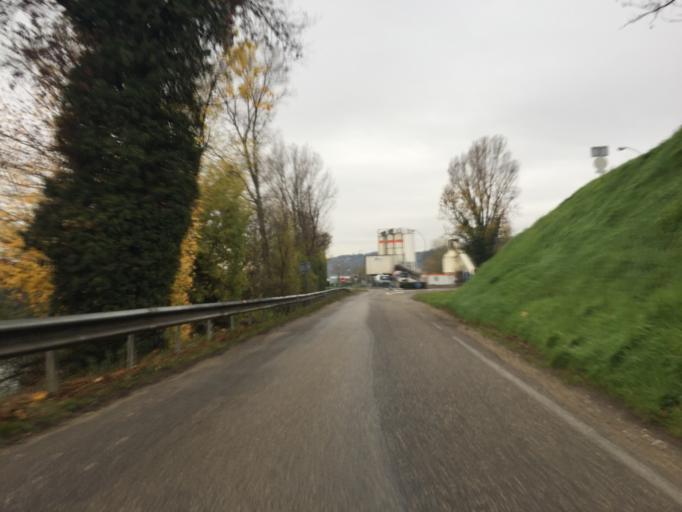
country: FR
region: Rhone-Alpes
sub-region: Departement de l'Ain
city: Miribel
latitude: 45.8199
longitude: 4.9473
